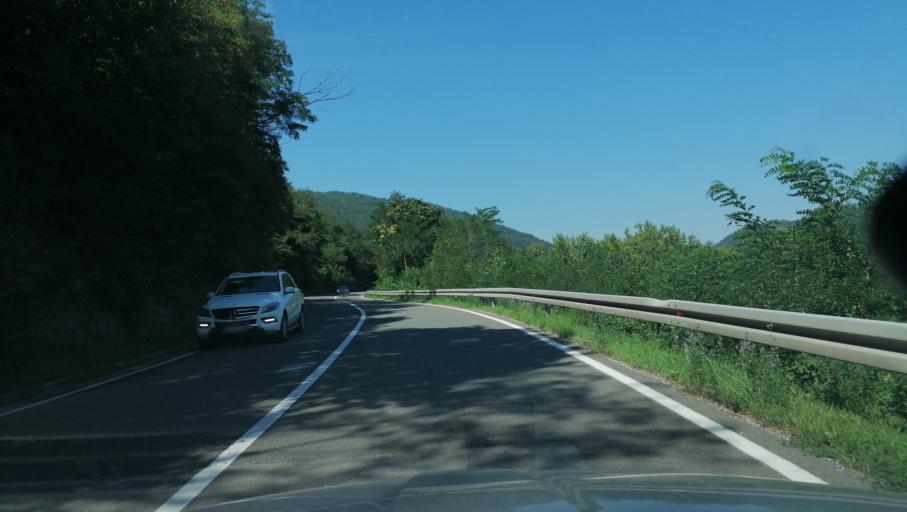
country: RS
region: Central Serbia
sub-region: Raski Okrug
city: Kraljevo
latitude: 43.6417
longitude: 20.5519
